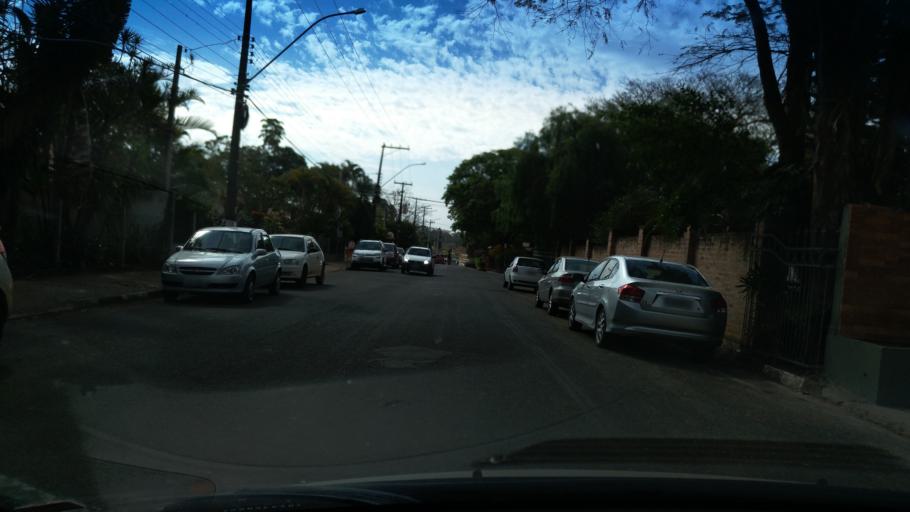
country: BR
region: Sao Paulo
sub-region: Jaguariuna
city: Jaguariuna
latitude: -22.6313
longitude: -47.0526
